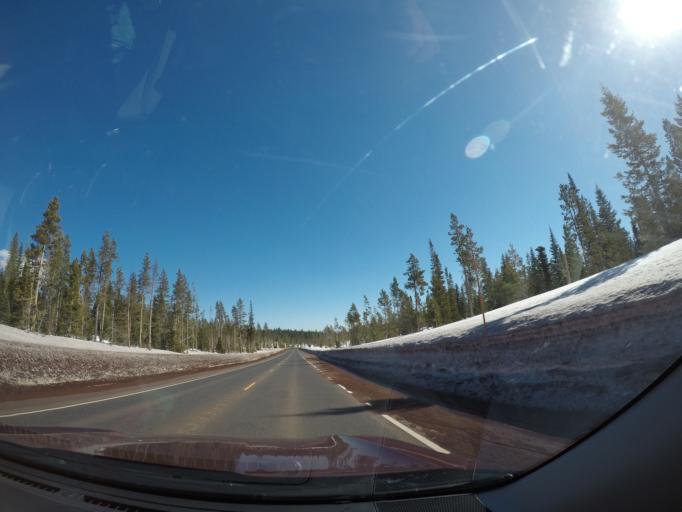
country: US
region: Oregon
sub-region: Deschutes County
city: Sunriver
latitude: 43.9871
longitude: -121.5716
